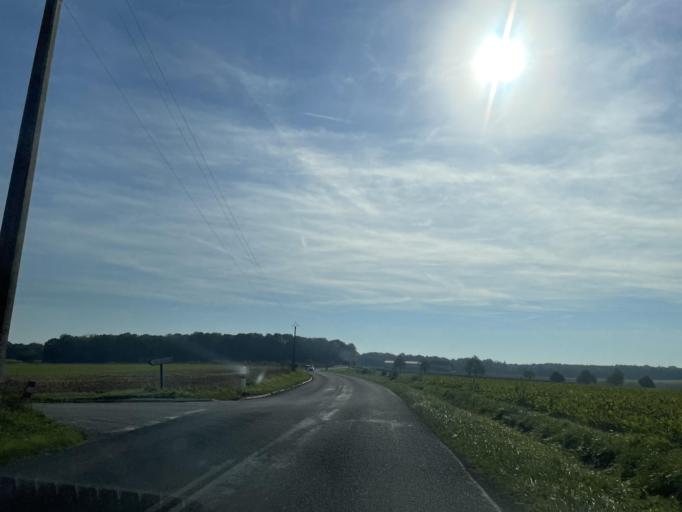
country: FR
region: Ile-de-France
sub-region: Departement de Seine-et-Marne
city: Saint-Jean-les-Deux-Jumeaux
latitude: 48.9259
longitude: 3.0013
